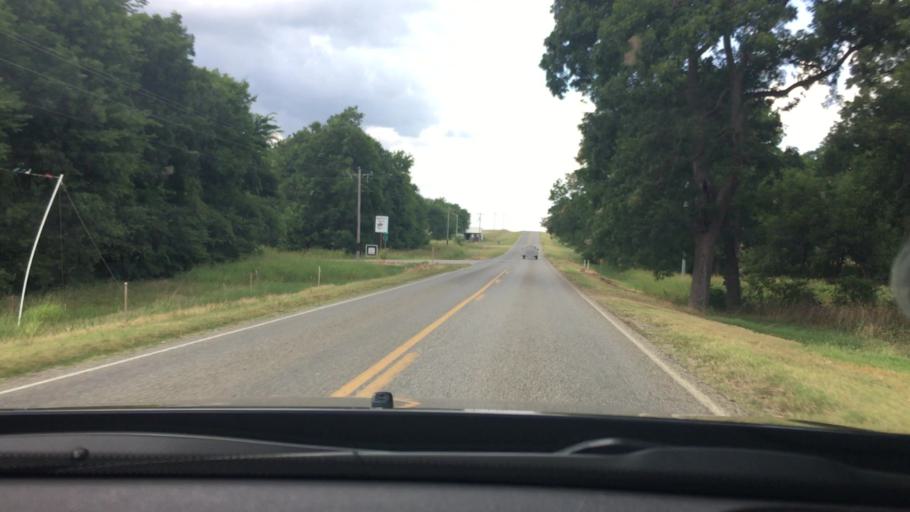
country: US
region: Oklahoma
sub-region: Pontotoc County
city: Ada
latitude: 34.5483
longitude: -96.6347
